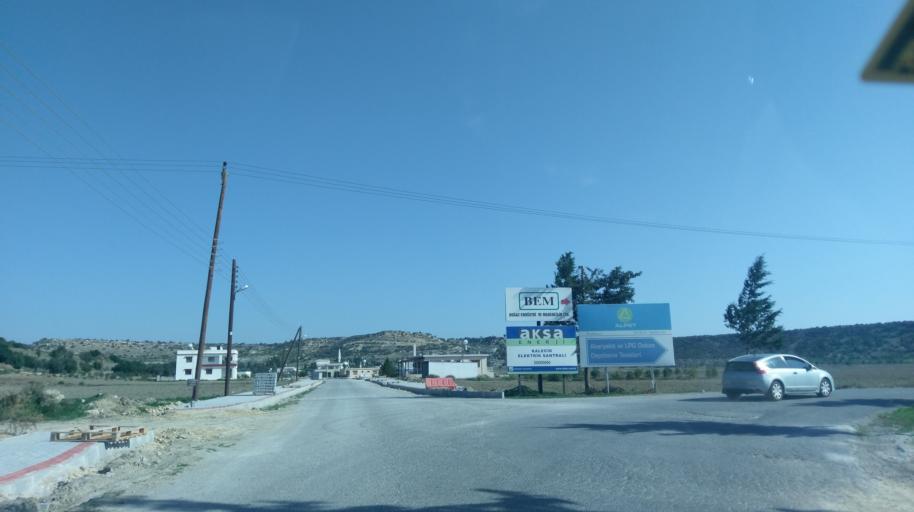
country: CY
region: Ammochostos
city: Trikomo
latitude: 35.3408
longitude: 33.9887
